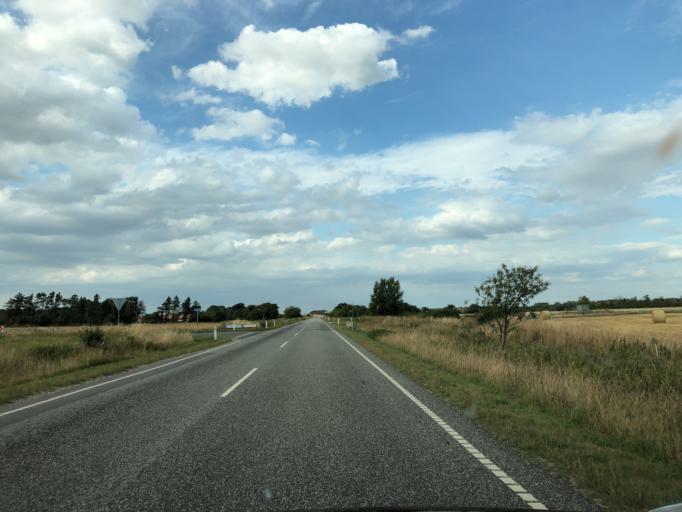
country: DK
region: Central Jutland
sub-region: Struer Kommune
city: Struer
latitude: 56.3958
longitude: 8.4593
